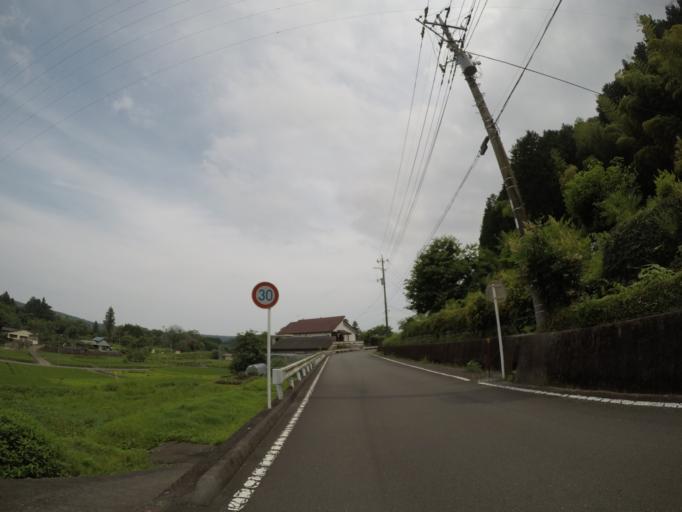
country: JP
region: Shizuoka
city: Fujinomiya
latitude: 35.2452
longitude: 138.5551
